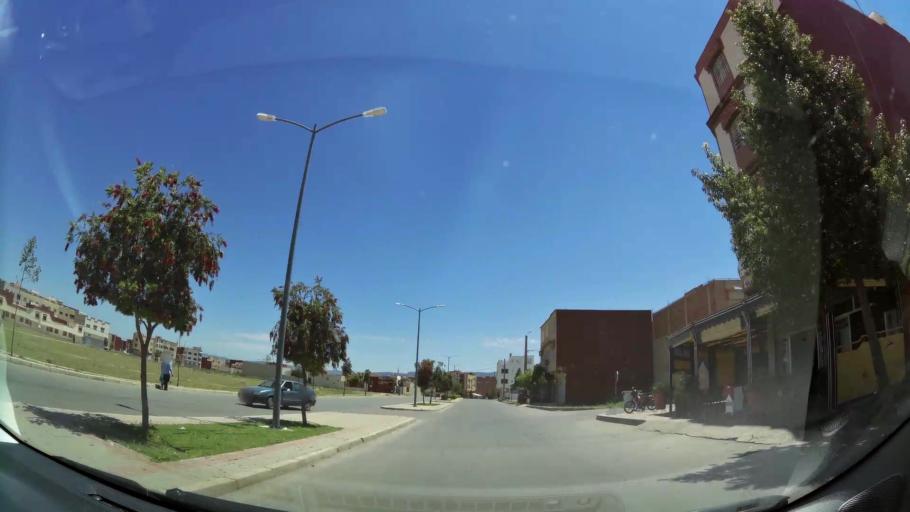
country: MA
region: Oriental
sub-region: Oujda-Angad
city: Oujda
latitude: 34.6829
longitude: -1.8726
